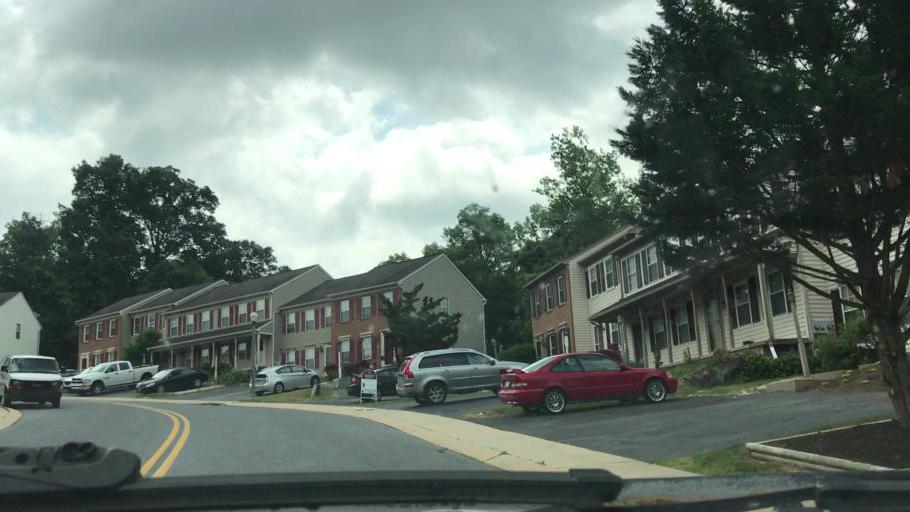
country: US
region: Pennsylvania
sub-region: Lancaster County
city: Elizabethtown
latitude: 40.1670
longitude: -76.6099
